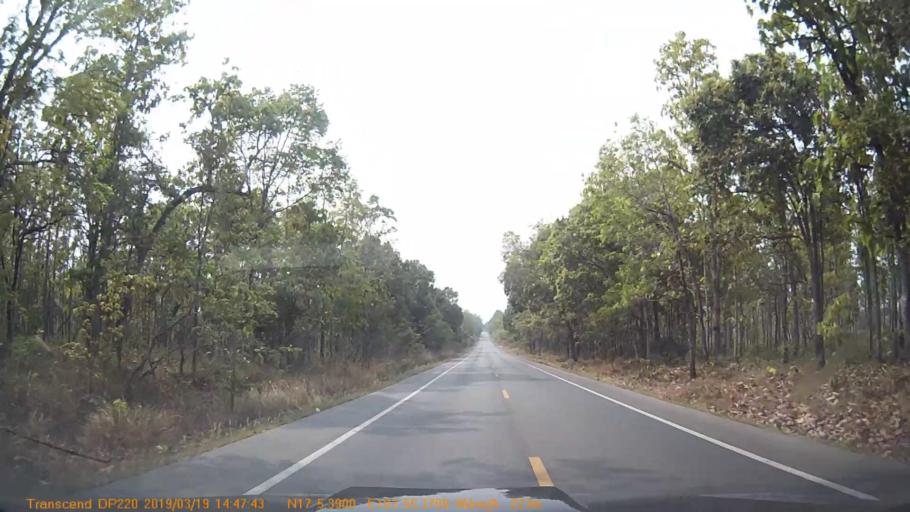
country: TH
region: Sakon Nakhon
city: Kut Bak
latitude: 17.0901
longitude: 103.9225
